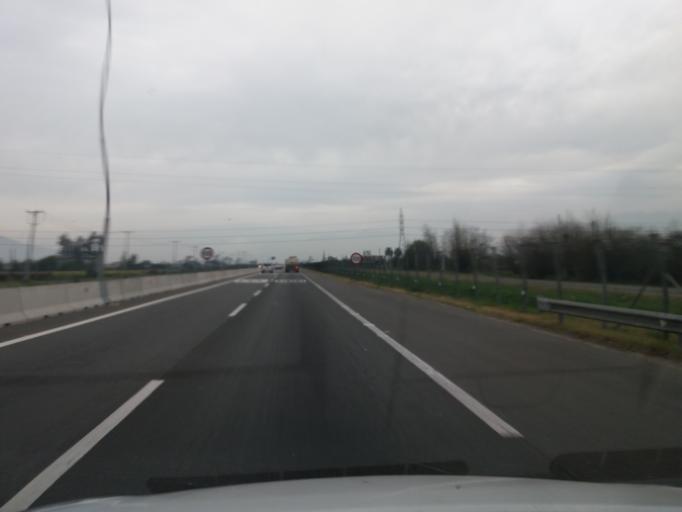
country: CL
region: Valparaiso
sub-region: Provincia de Quillota
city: Quillota
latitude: -32.9234
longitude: -71.2805
